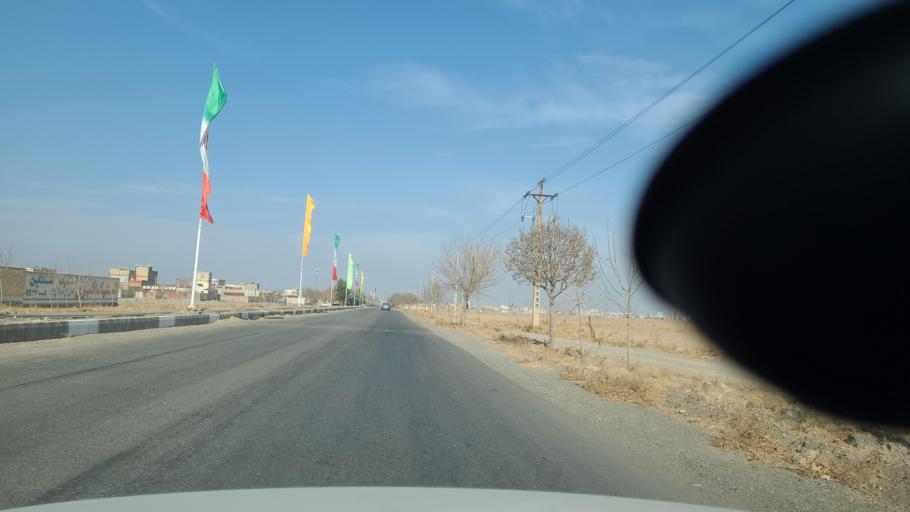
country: IR
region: Razavi Khorasan
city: Fariman
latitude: 35.6790
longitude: 59.8430
